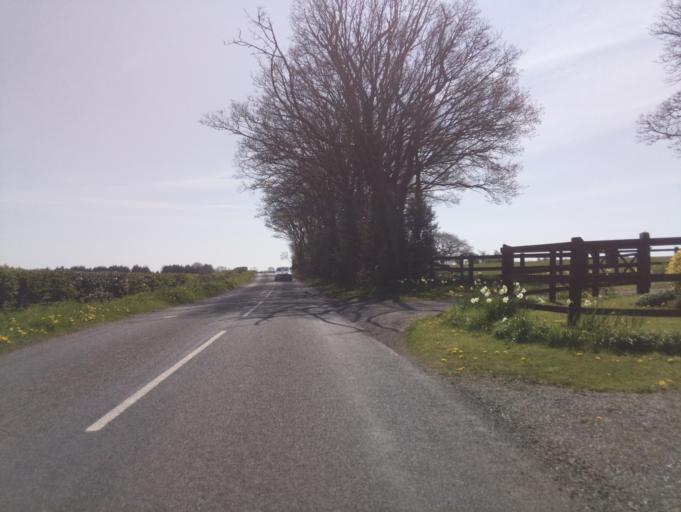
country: GB
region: Wales
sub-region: Newport
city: Llanvaches
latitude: 51.6617
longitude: -2.7975
